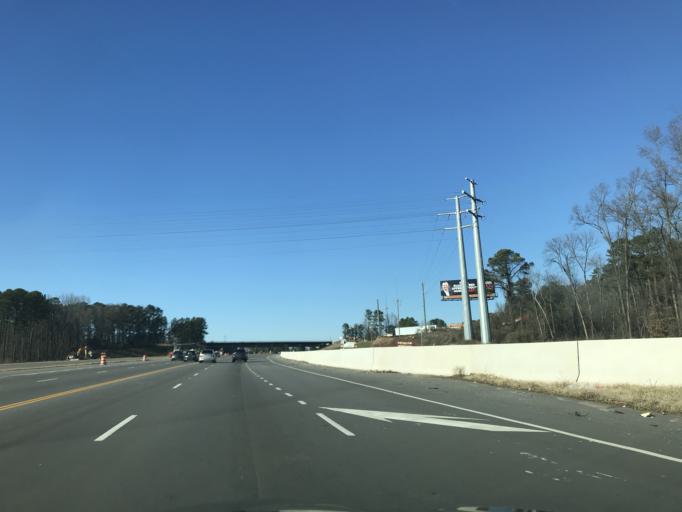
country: US
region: North Carolina
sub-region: Durham County
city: Durham
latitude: 35.9821
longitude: -78.8577
